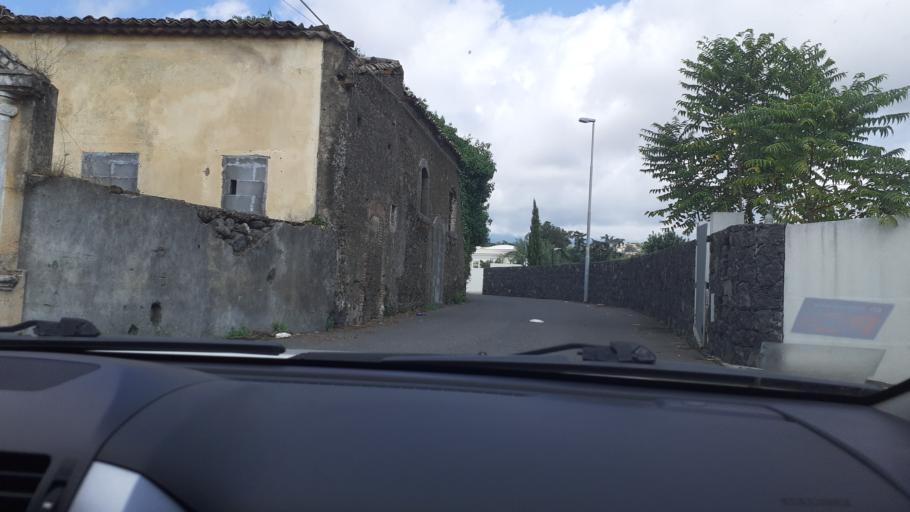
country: IT
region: Sicily
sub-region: Catania
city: San Giovanni la Punta
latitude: 37.5925
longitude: 15.0820
